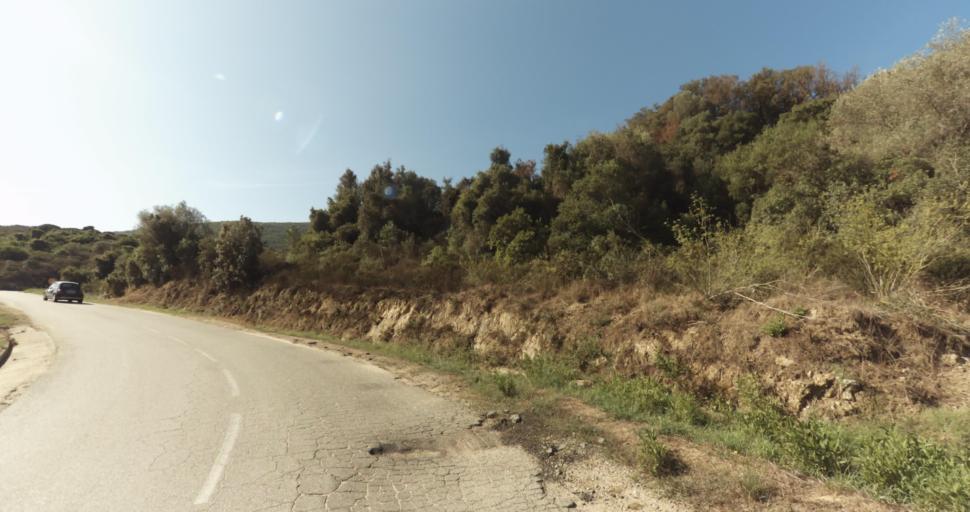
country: FR
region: Corsica
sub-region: Departement de la Corse-du-Sud
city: Ajaccio
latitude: 41.9340
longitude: 8.6796
